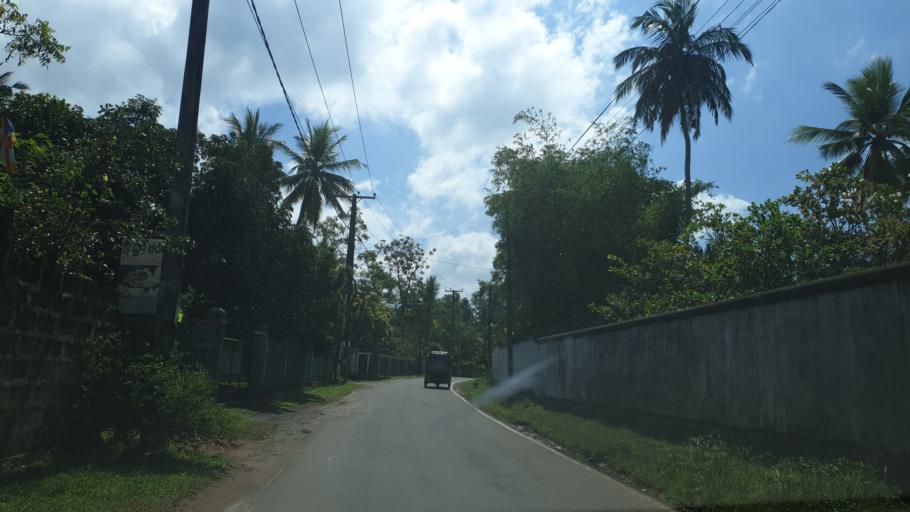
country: LK
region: Western
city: Panadura
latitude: 6.6807
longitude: 79.9295
